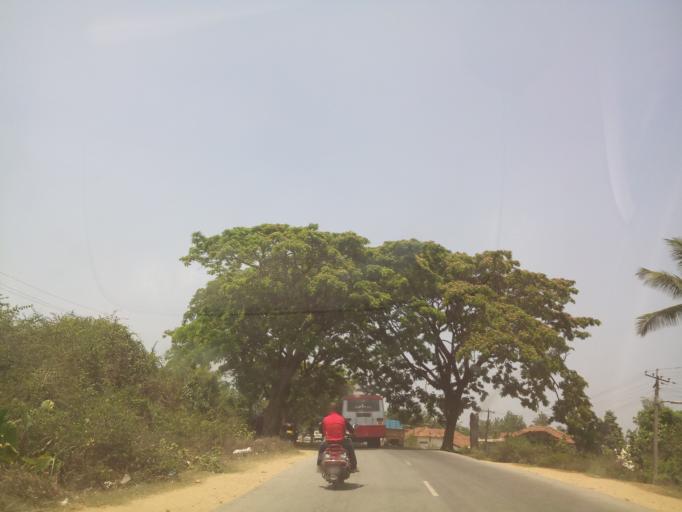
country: IN
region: Karnataka
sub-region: Hassan
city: Alur
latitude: 12.9448
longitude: 75.8941
